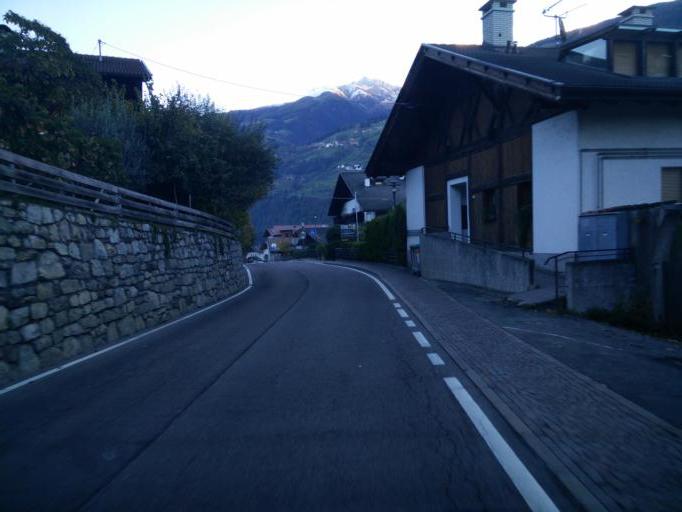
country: IT
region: Trentino-Alto Adige
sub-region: Bolzano
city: Rifiano
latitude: 46.7033
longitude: 11.1813
